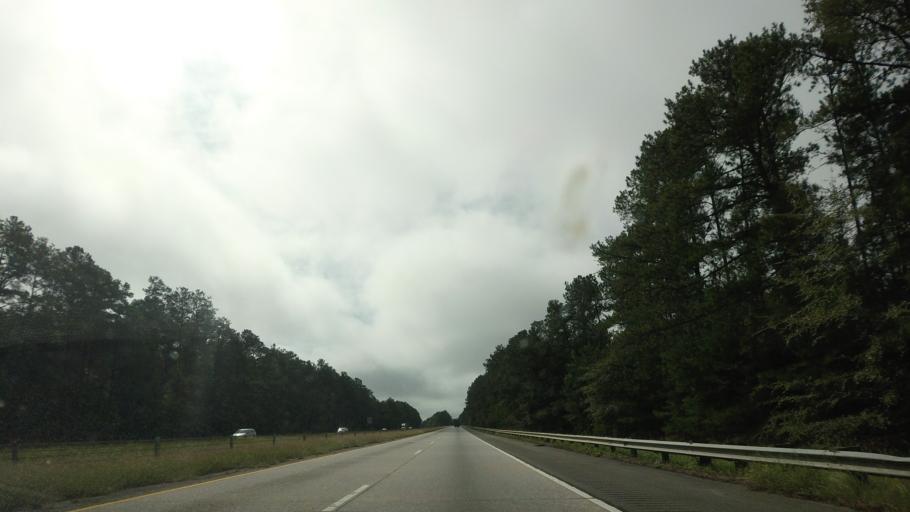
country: US
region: Georgia
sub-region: Bibb County
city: Macon
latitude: 32.7712
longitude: -83.5576
